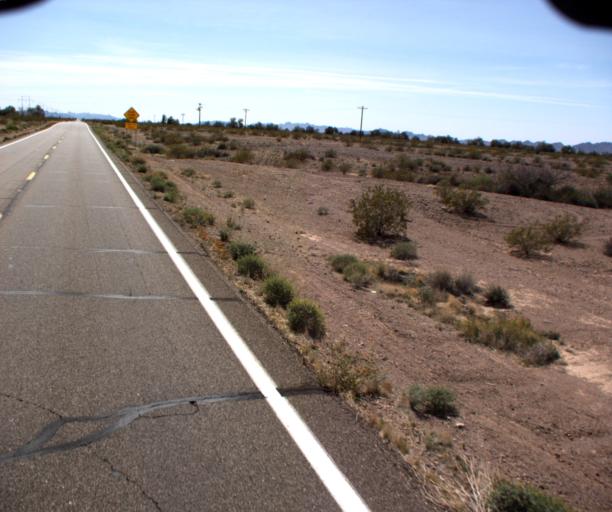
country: US
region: Arizona
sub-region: La Paz County
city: Quartzsite
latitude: 33.4976
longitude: -114.2170
